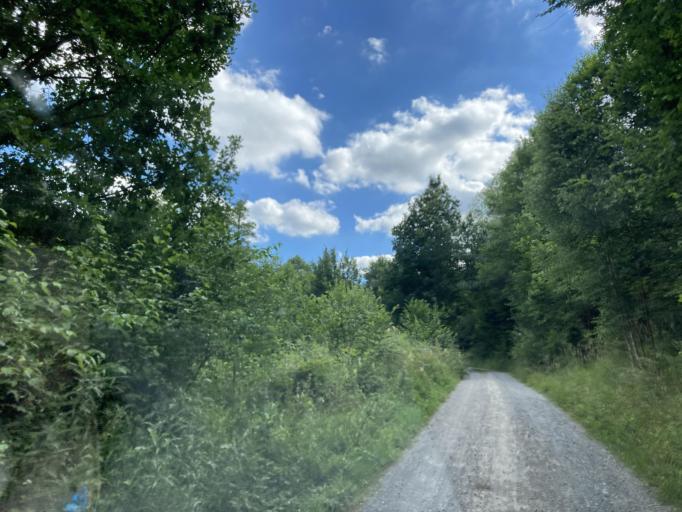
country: DE
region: Baden-Wuerttemberg
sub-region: Tuebingen Region
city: Ofterdingen
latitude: 48.4448
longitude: 9.0208
